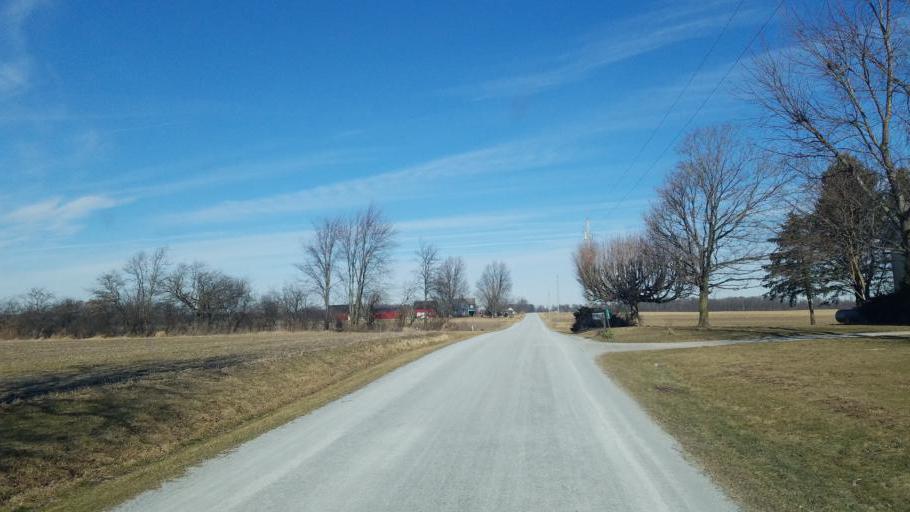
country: US
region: Ohio
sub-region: Hardin County
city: Kenton
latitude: 40.5712
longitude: -83.4687
